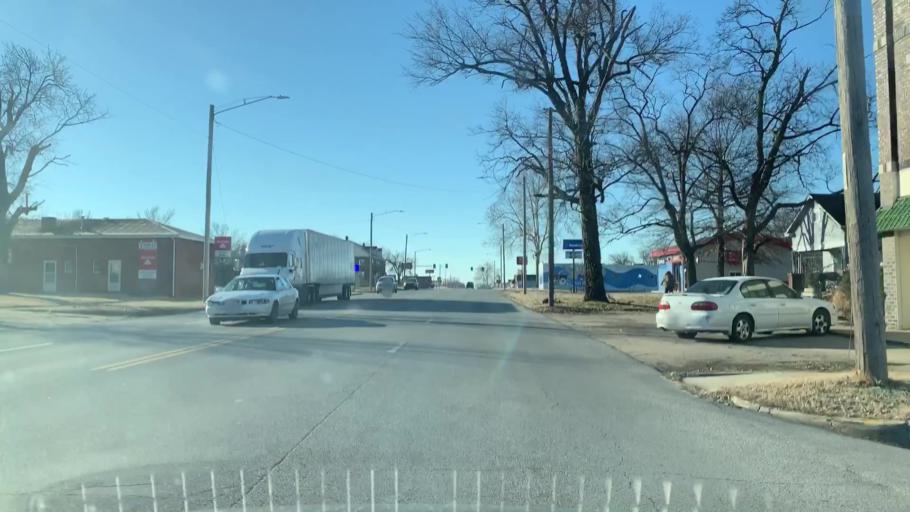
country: US
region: Kansas
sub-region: Crawford County
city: Pittsburg
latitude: 37.4023
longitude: -94.7050
